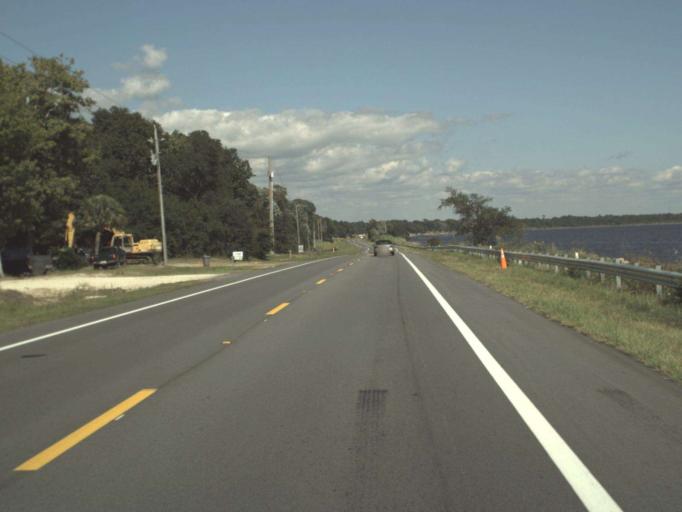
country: US
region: Florida
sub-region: Walton County
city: Miramar Beach
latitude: 30.4709
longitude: -86.3418
